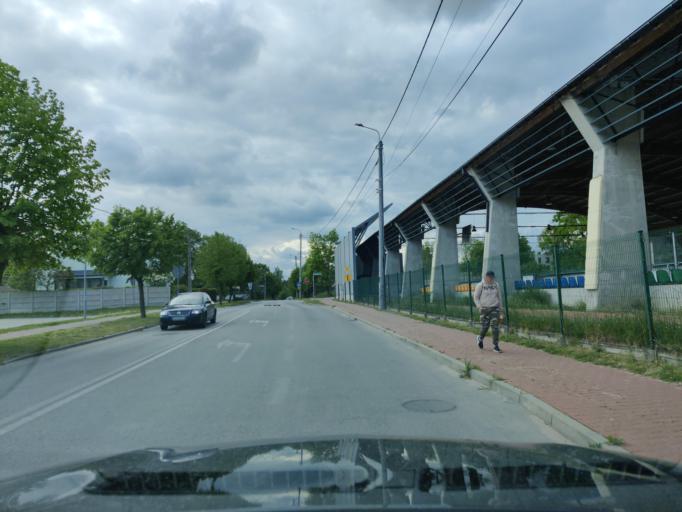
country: PL
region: Swietokrzyskie
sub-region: Powiat skarzyski
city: Skarzysko-Kamienna
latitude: 51.1189
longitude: 20.8599
